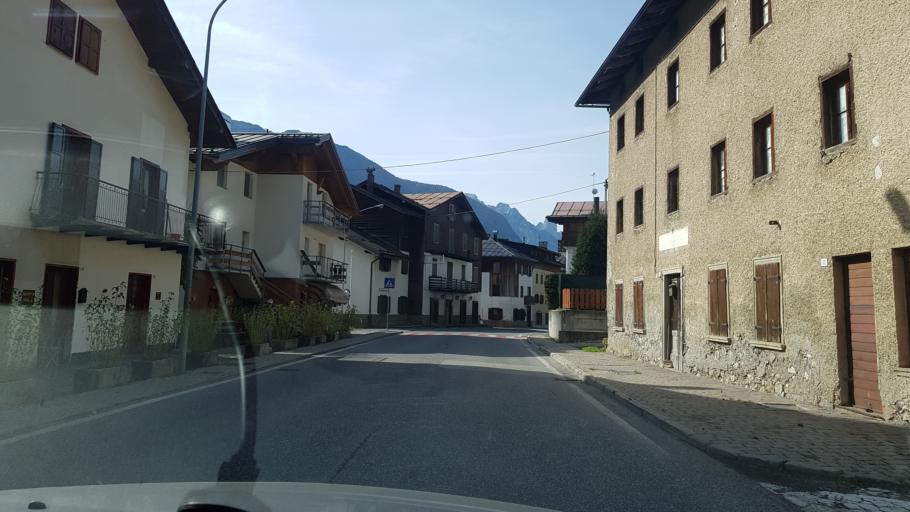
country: IT
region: Veneto
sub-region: Provincia di Belluno
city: San Pietro di Cadore
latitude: 46.5752
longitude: 12.6004
